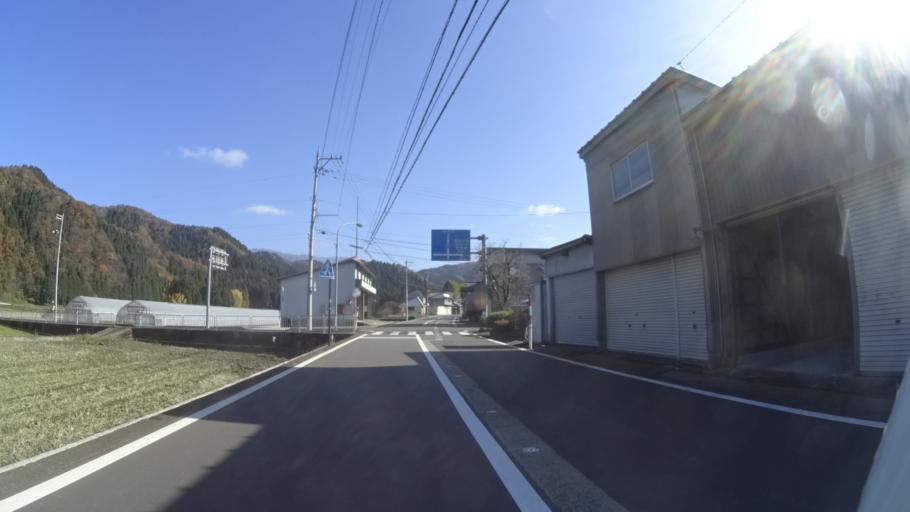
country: JP
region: Fukui
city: Sabae
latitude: 35.8796
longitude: 136.3436
